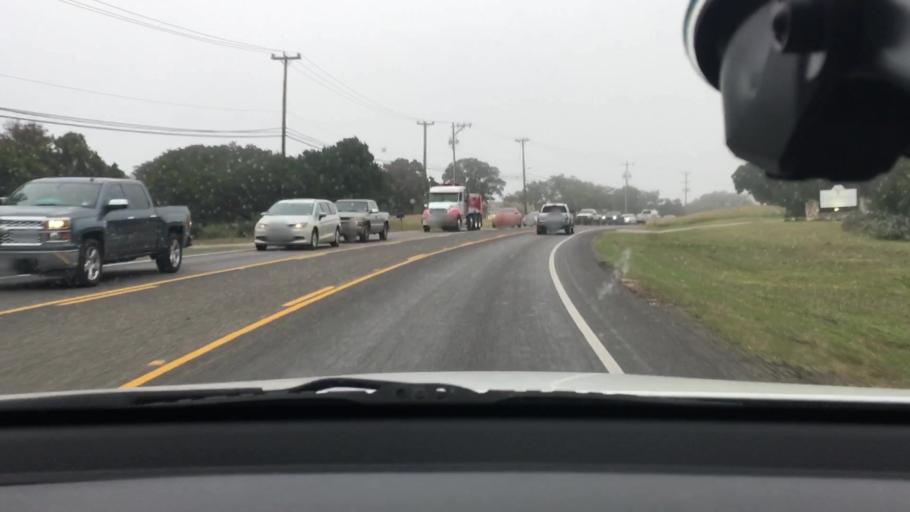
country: US
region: Texas
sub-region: Comal County
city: Garden Ridge
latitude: 29.6217
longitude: -98.3019
